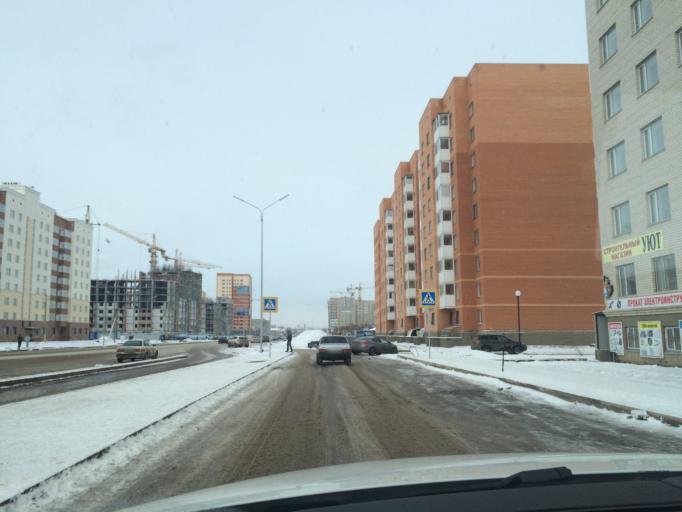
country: KZ
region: Astana Qalasy
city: Astana
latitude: 51.1254
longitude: 71.5002
